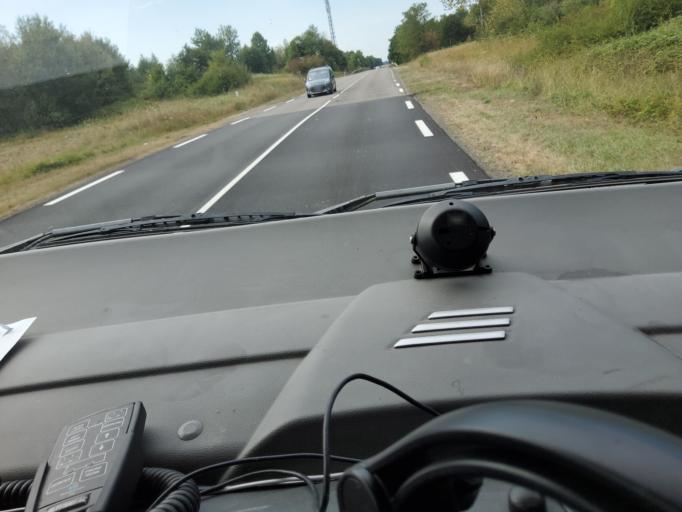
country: FR
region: Franche-Comte
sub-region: Departement du Jura
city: Mont-sous-Vaudrey
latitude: 46.9780
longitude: 5.5109
